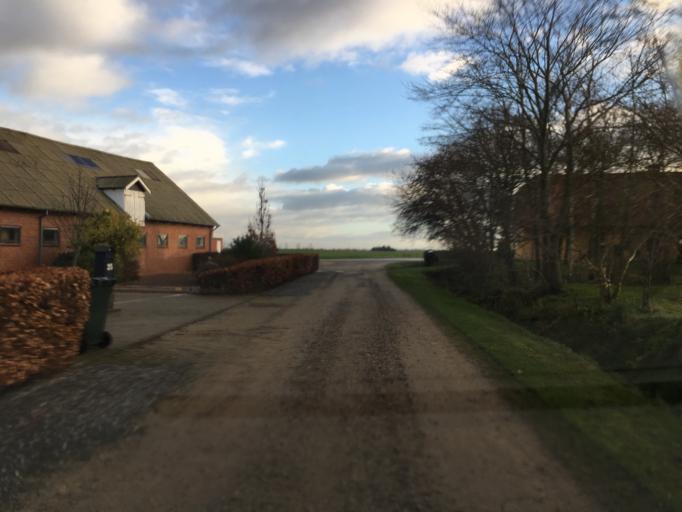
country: DK
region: South Denmark
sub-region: Tonder Kommune
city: Sherrebek
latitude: 55.1730
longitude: 8.8088
